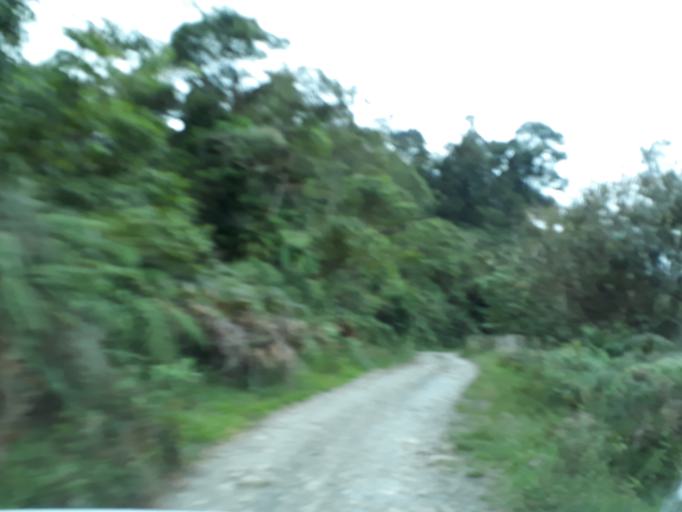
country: CO
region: Boyaca
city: Muzo
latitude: 5.3820
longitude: -74.0800
